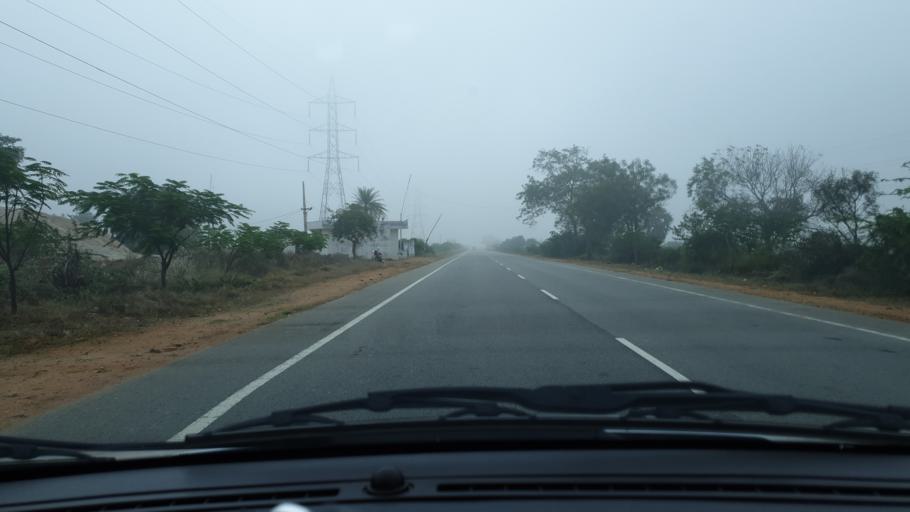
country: IN
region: Telangana
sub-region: Nalgonda
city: Devarkonda
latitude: 16.6269
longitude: 78.6655
